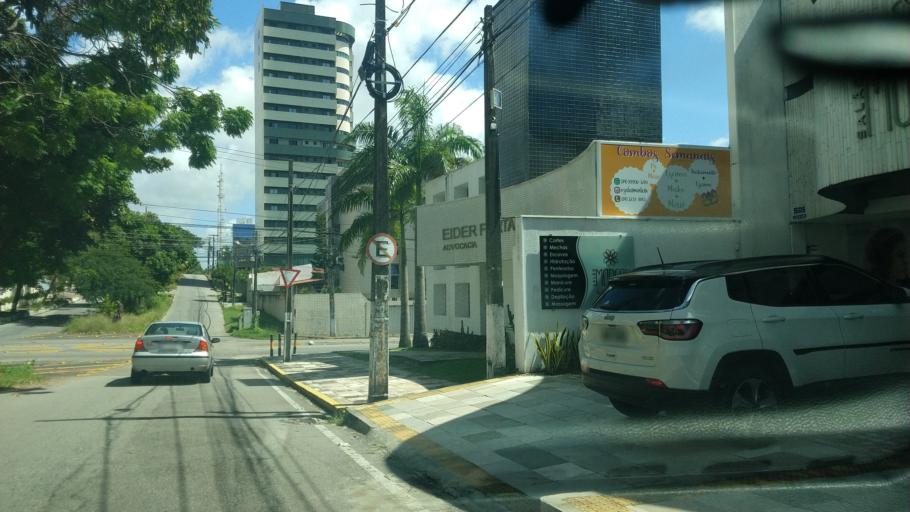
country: BR
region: Rio Grande do Norte
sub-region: Natal
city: Natal
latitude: -5.8310
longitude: -35.2192
